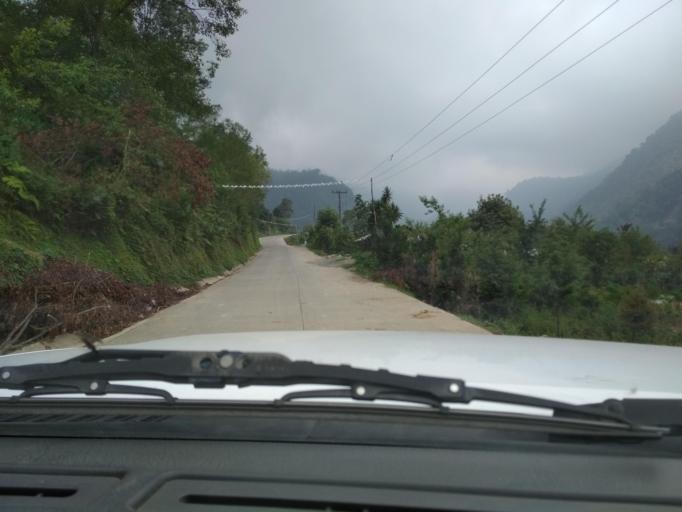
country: MX
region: Veracruz
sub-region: La Perla
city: Metlac Hernandez (Metlac Primero)
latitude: 18.9783
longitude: -97.1365
